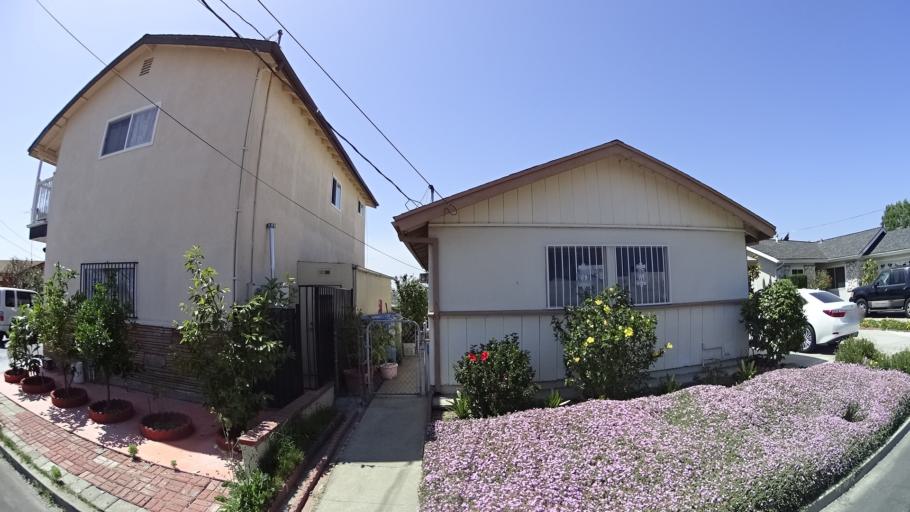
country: US
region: California
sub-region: Los Angeles County
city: Boyle Heights
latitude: 34.0691
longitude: -118.2042
